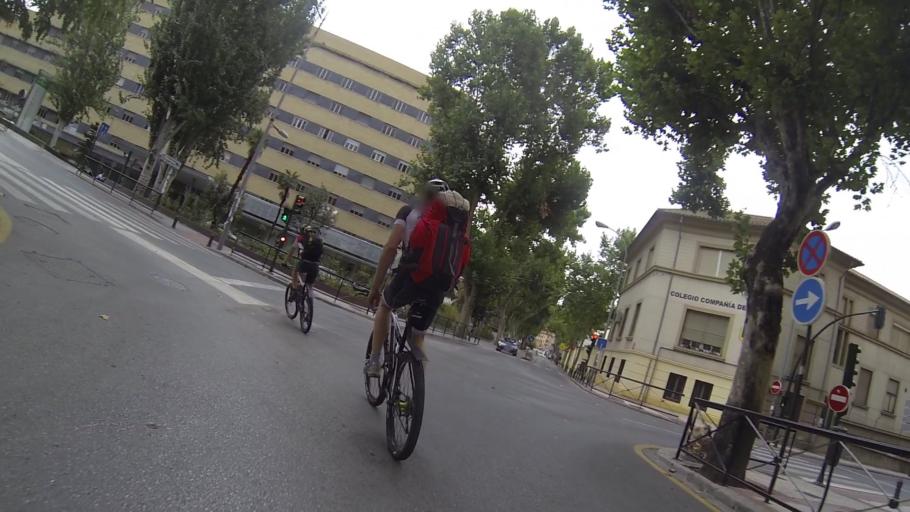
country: ES
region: Andalusia
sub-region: Provincia de Granada
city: Granada
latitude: 37.1891
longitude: -3.6118
